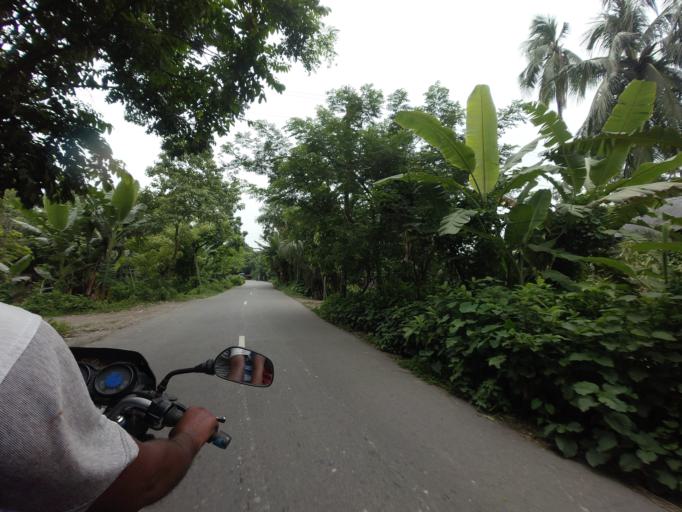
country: BD
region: Khulna
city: Kalia
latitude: 23.1605
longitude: 89.6440
